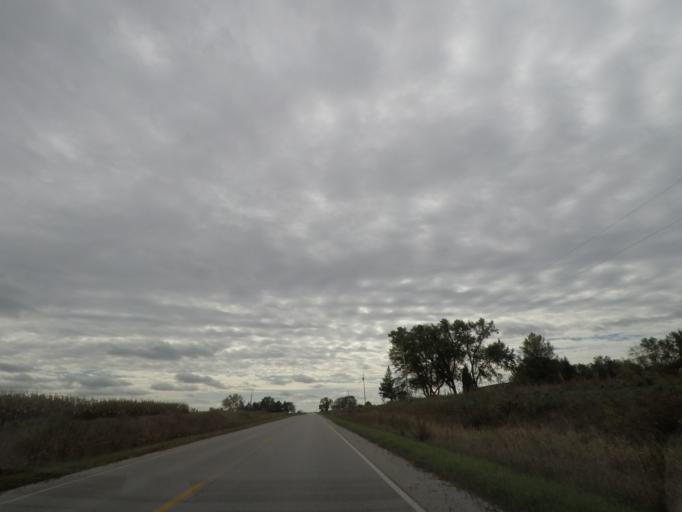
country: US
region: Iowa
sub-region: Story County
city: Huxley
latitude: 41.8664
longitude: -93.5316
